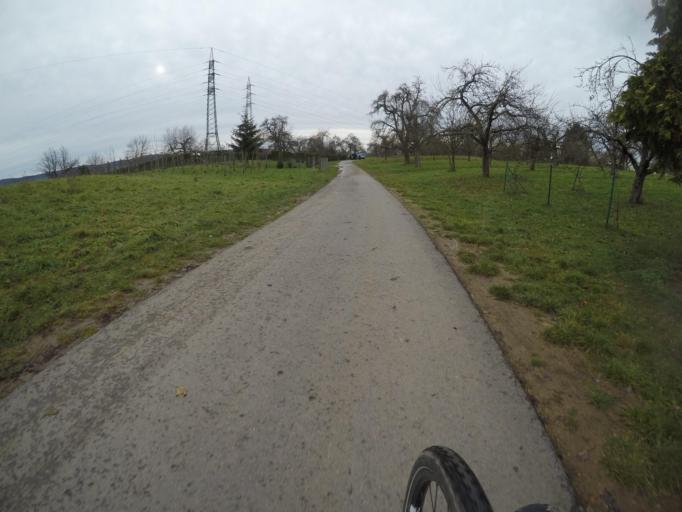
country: DE
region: Baden-Wuerttemberg
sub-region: Regierungsbezirk Stuttgart
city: Korb
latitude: 48.8452
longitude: 9.3390
